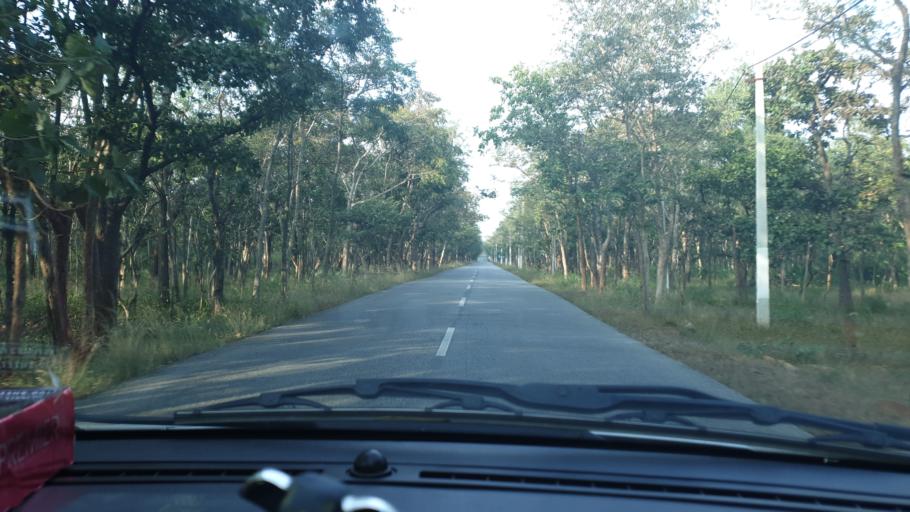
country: IN
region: Andhra Pradesh
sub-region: Kurnool
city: Srisailam
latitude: 16.2940
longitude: 78.7308
